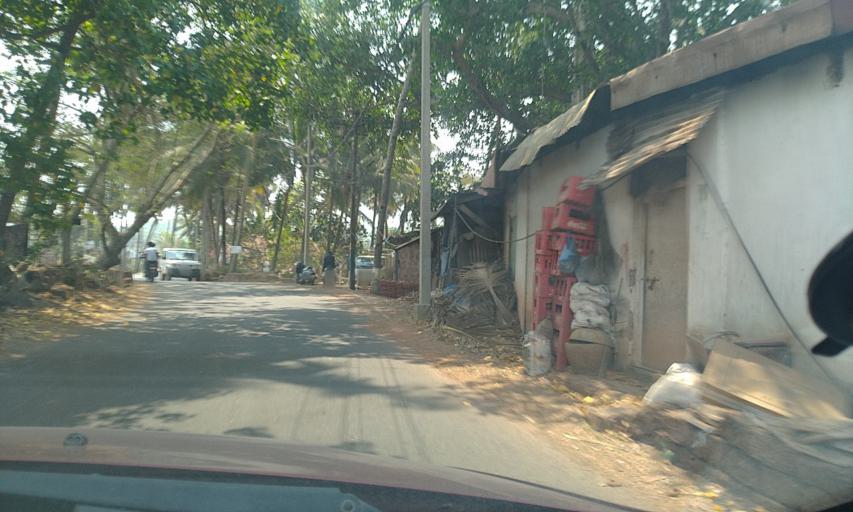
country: IN
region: Goa
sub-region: North Goa
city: Vagator
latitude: 15.5923
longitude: 73.7622
